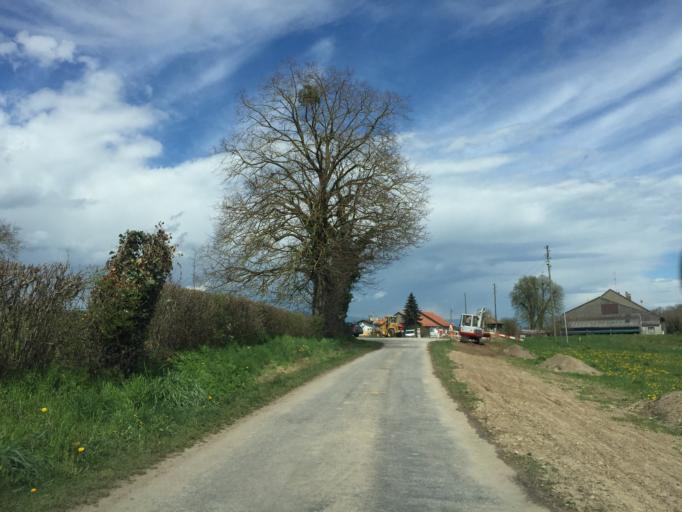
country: CH
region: Vaud
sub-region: Morges District
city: La Chaux
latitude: 46.6196
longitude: 6.4739
